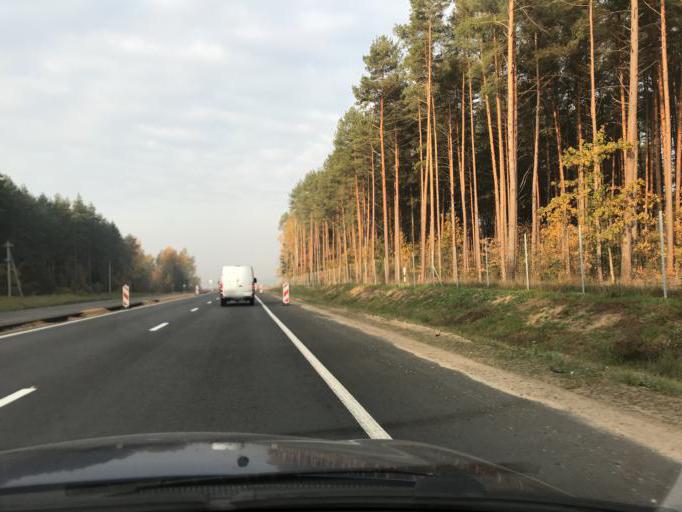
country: BY
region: Grodnenskaya
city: Lida
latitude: 53.8292
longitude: 25.3840
